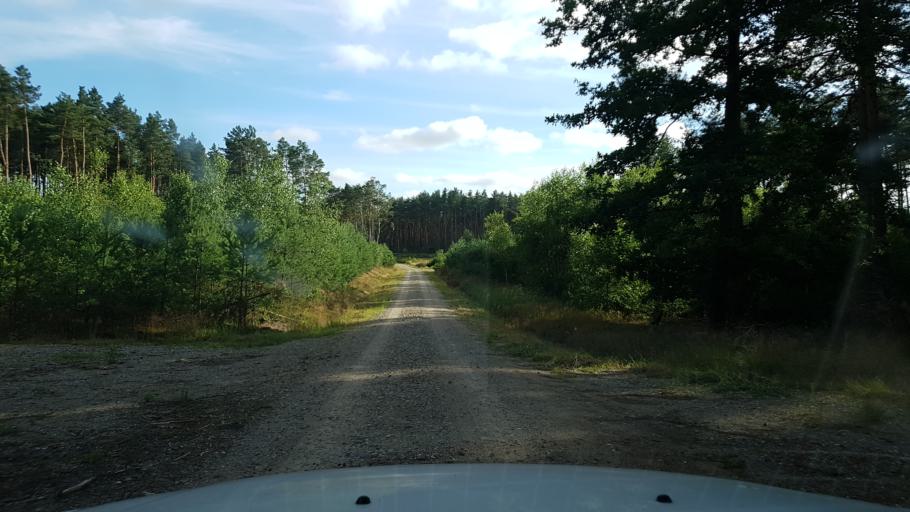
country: PL
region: West Pomeranian Voivodeship
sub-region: Powiat kolobrzeski
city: Grzybowo
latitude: 54.0977
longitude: 15.5357
